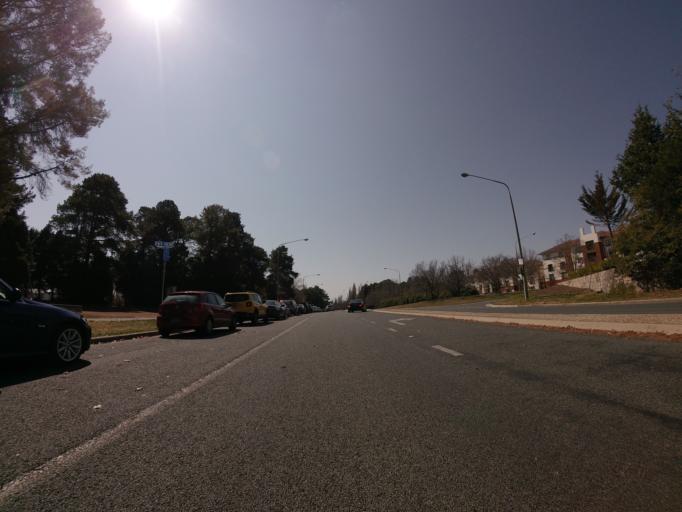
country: AU
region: Australian Capital Territory
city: Canberra
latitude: -35.2993
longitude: 149.1224
